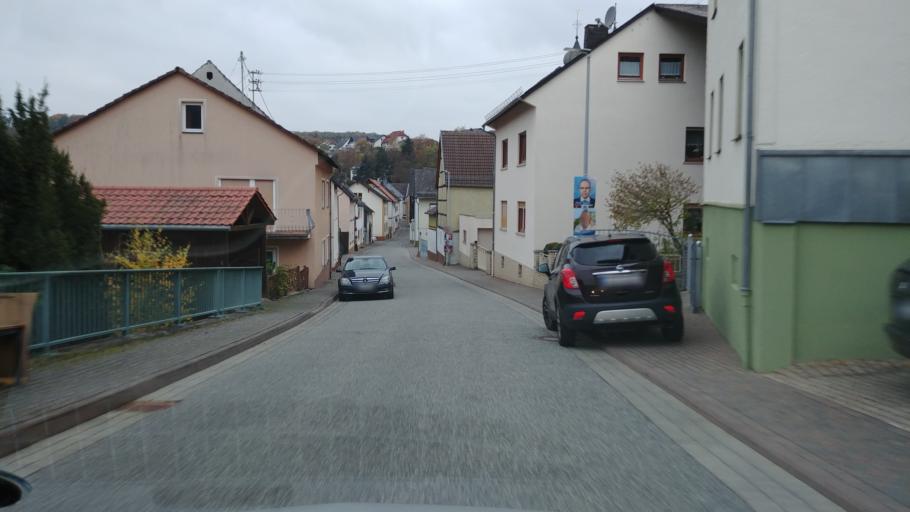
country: DE
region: Rheinland-Pfalz
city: Burgschwalbach
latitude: 50.2283
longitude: 8.1227
